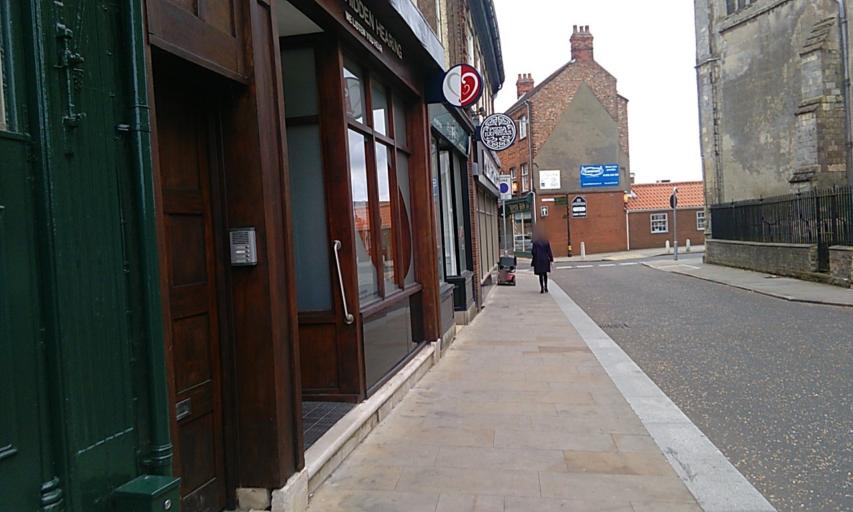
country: GB
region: England
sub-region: Norfolk
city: King's Lynn
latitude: 52.7520
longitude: 0.3958
